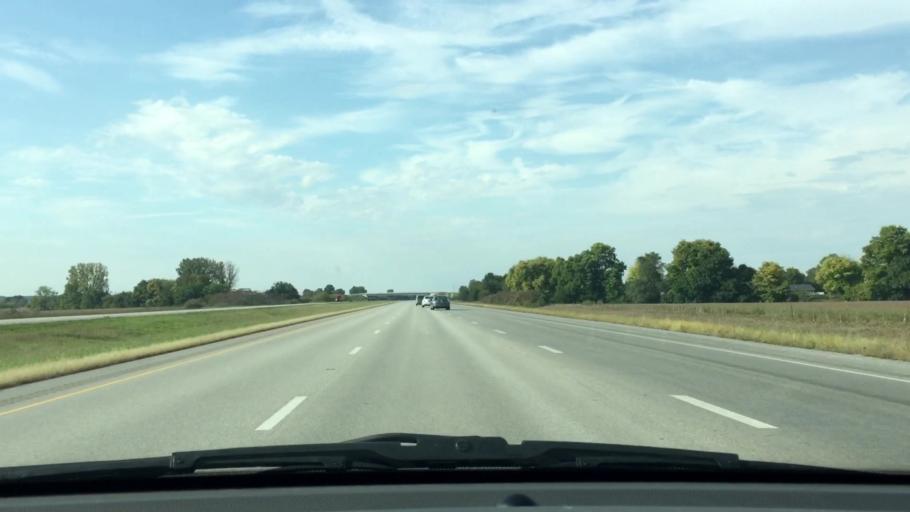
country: US
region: Illinois
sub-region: Rock Island County
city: Port Byron
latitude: 41.5538
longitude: -90.2459
